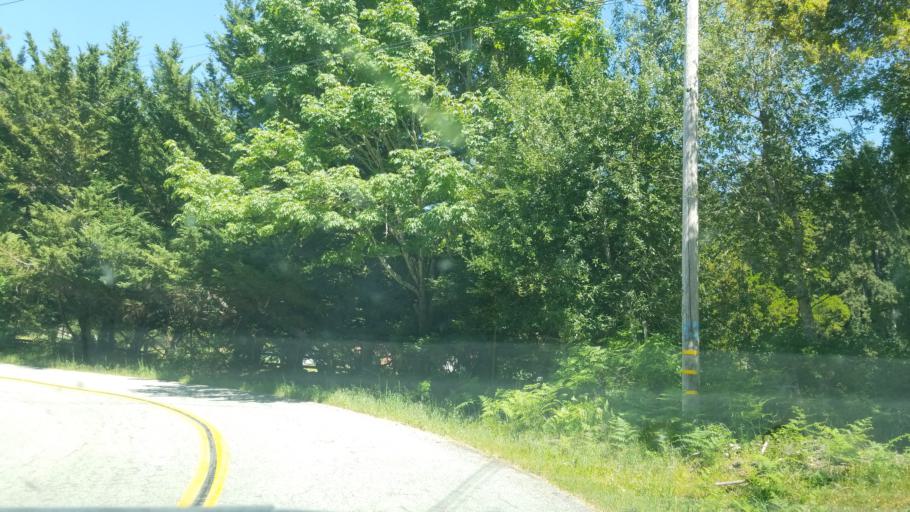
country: US
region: California
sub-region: Santa Cruz County
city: Day Valley
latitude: 37.0489
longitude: -121.8073
